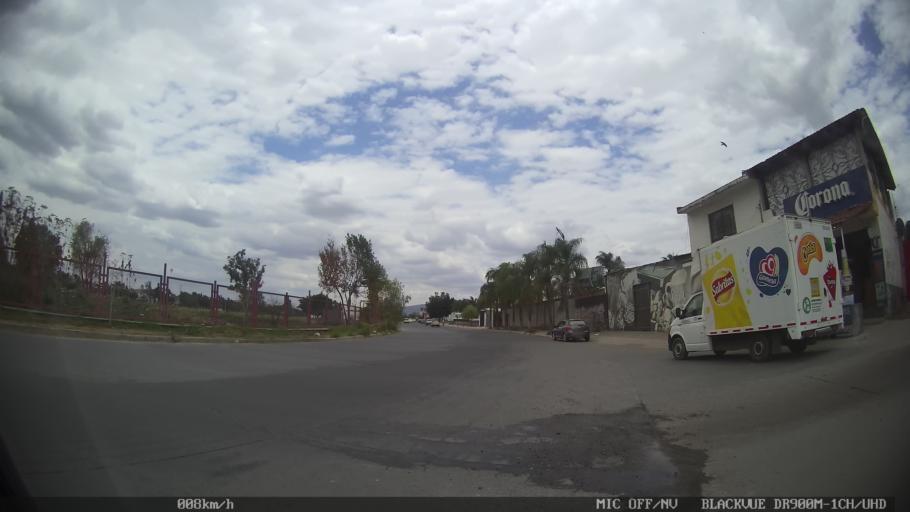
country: MX
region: Jalisco
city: Tlaquepaque
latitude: 20.6487
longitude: -103.2699
